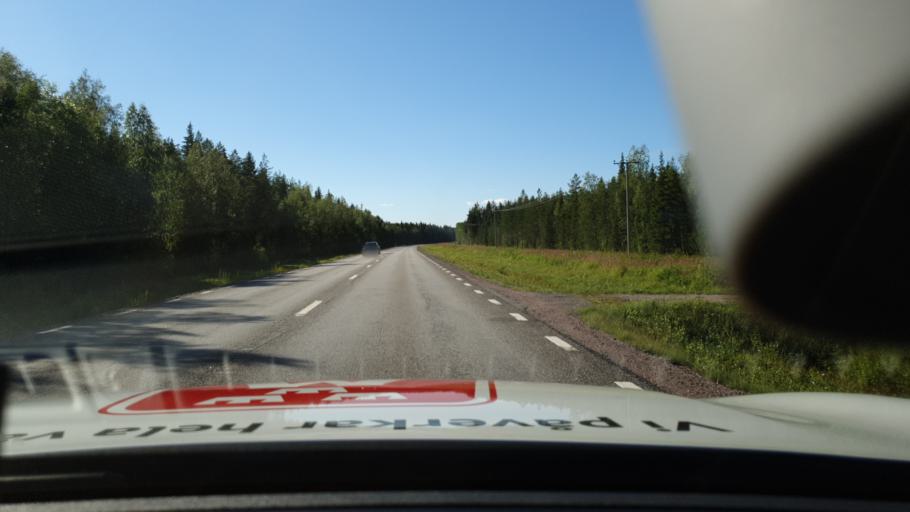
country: SE
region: Norrbotten
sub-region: Pitea Kommun
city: Rosvik
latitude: 65.5824
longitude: 21.6840
